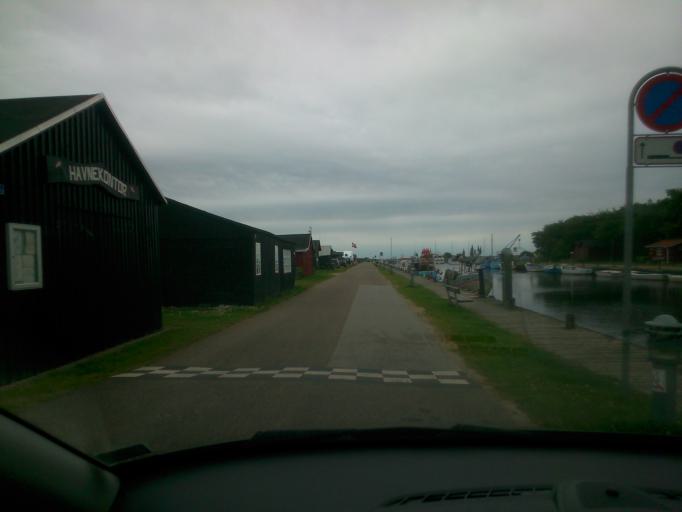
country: DK
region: Central Jutland
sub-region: Ringkobing-Skjern Kommune
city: Skjern
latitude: 55.9547
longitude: 8.3731
